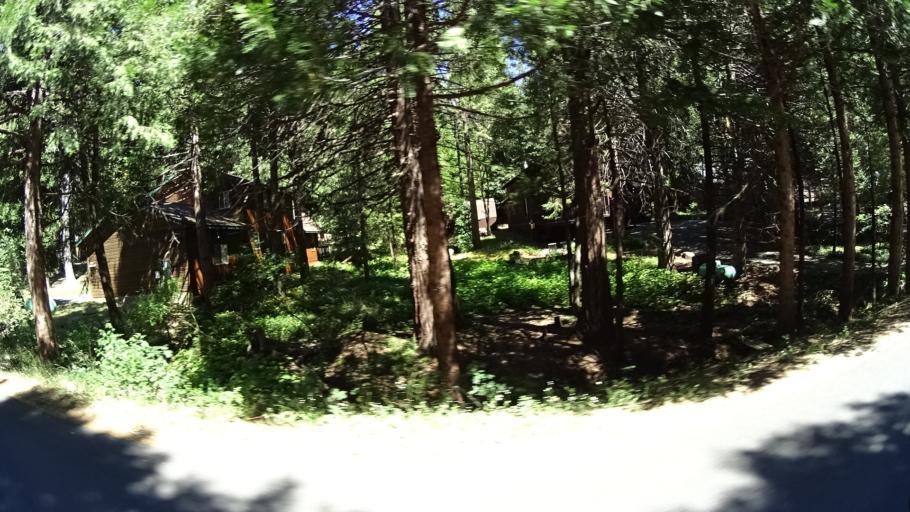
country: US
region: California
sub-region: Calaveras County
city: Arnold
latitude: 38.2929
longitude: -120.2810
